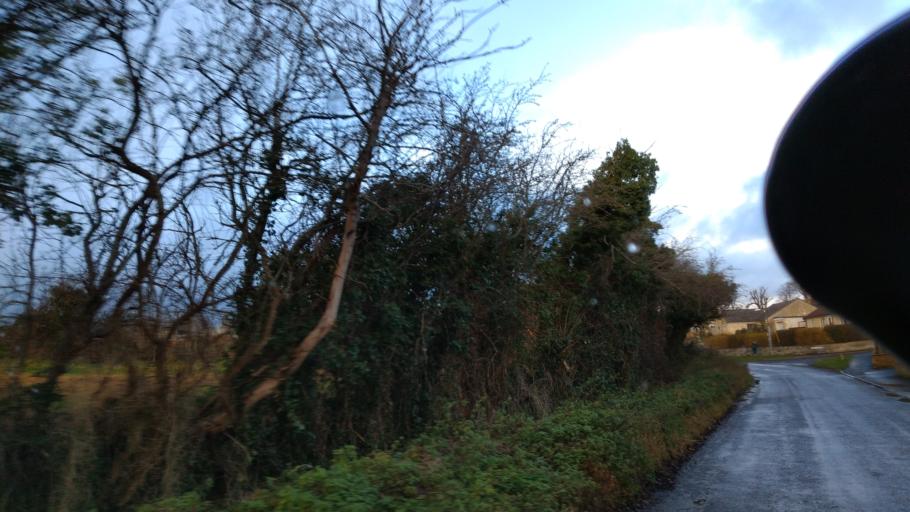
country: GB
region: England
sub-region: Wiltshire
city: Atworth
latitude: 51.3939
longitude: -2.1675
